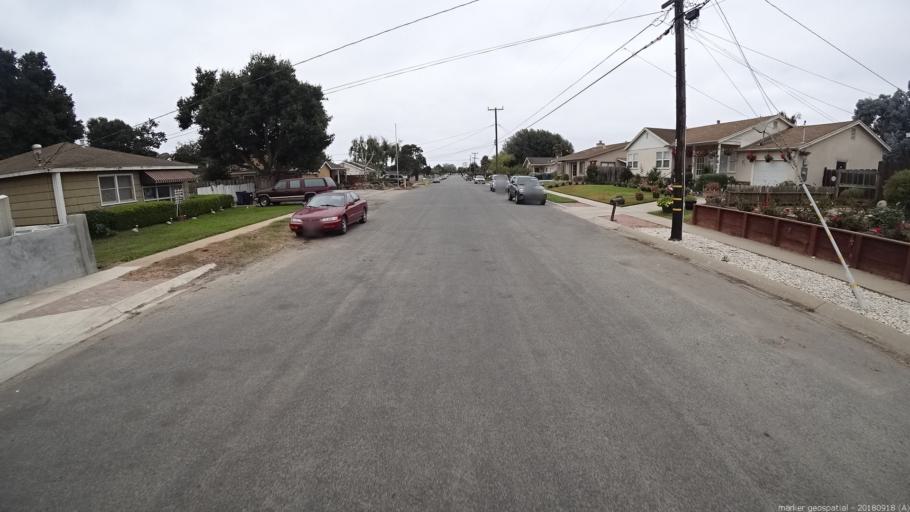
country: US
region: California
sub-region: Monterey County
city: Prunedale
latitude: 36.7367
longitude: -121.6376
